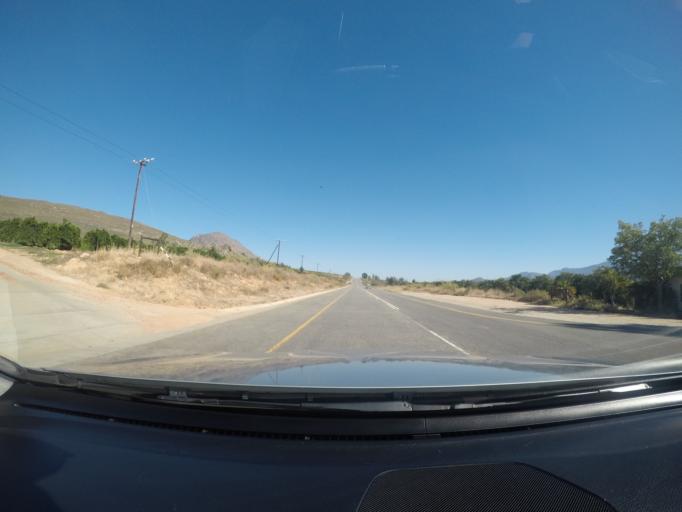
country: ZA
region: Western Cape
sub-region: West Coast District Municipality
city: Clanwilliam
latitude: -32.5480
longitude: 18.9803
